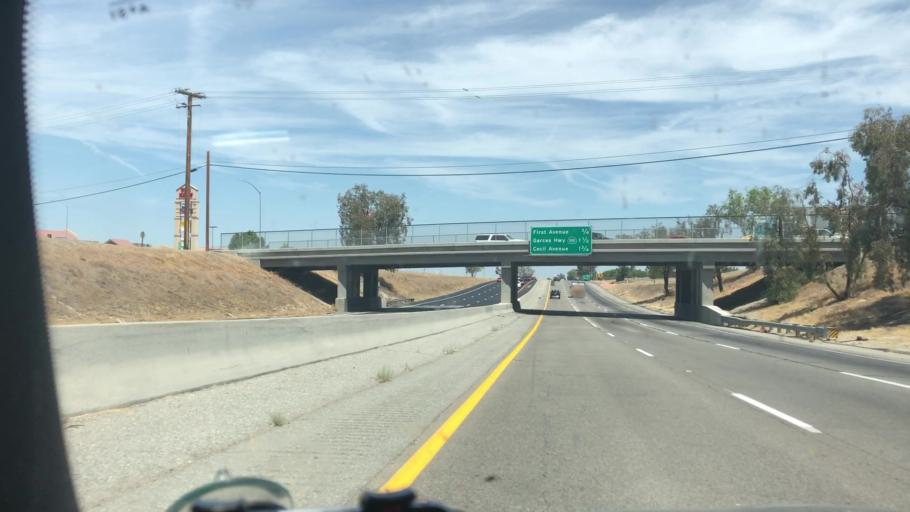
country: US
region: California
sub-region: Kern County
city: Delano
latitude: 35.7461
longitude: -119.2434
